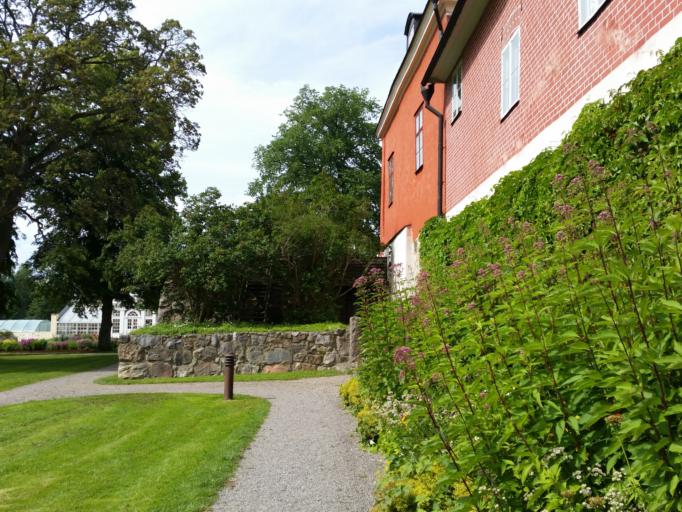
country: SE
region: Soedermanland
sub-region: Strangnas Kommun
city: Mariefred
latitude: 59.2560
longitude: 17.2187
